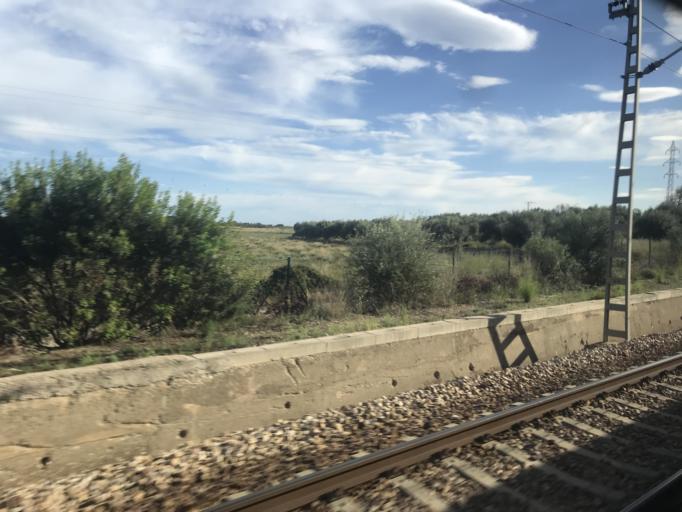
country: ES
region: Valencia
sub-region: Provincia de Castello
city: Torreblanca
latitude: 40.2357
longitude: 0.2236
